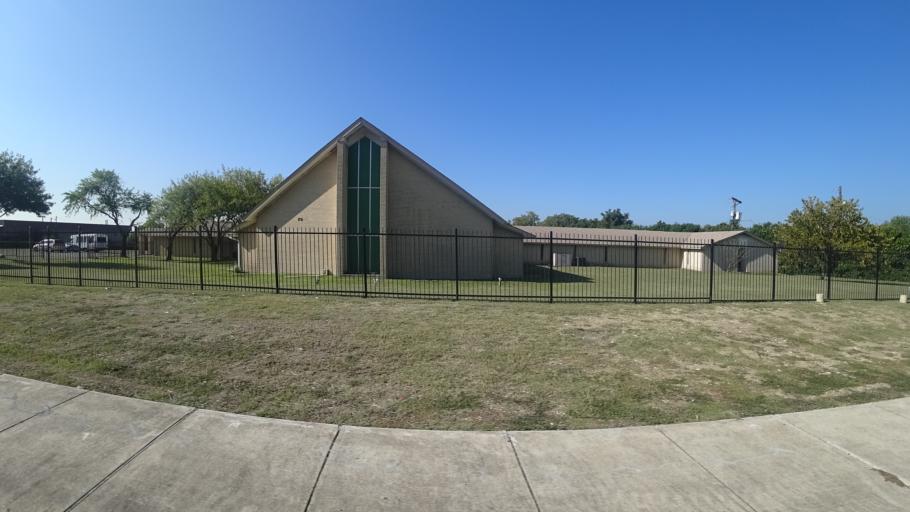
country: US
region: Texas
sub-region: Travis County
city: Austin
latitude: 30.3236
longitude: -97.6717
